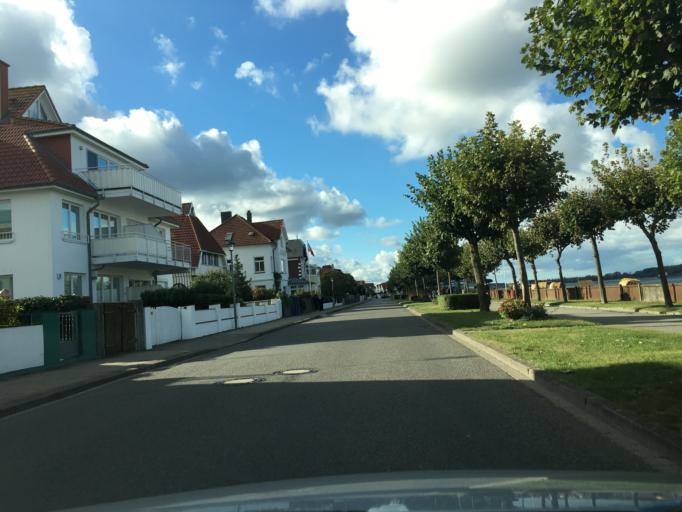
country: DE
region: Schleswig-Holstein
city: Laboe
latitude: 54.4097
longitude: 10.2254
